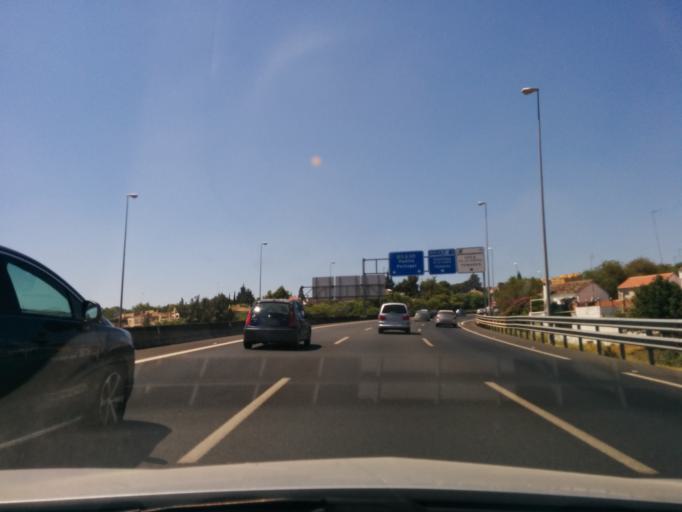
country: ES
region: Andalusia
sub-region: Provincia de Sevilla
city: Tomares
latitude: 37.3822
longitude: -6.0355
